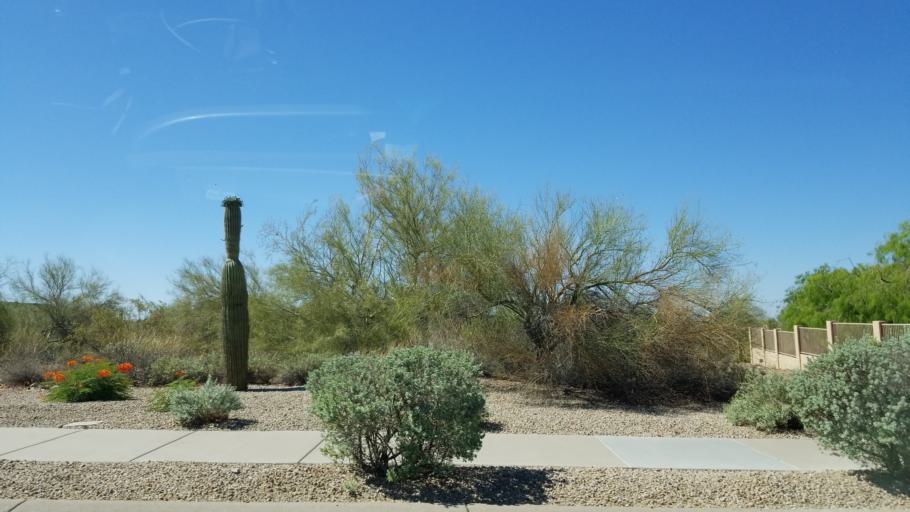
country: US
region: Arizona
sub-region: Maricopa County
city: Fountain Hills
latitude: 33.5896
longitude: -111.7971
